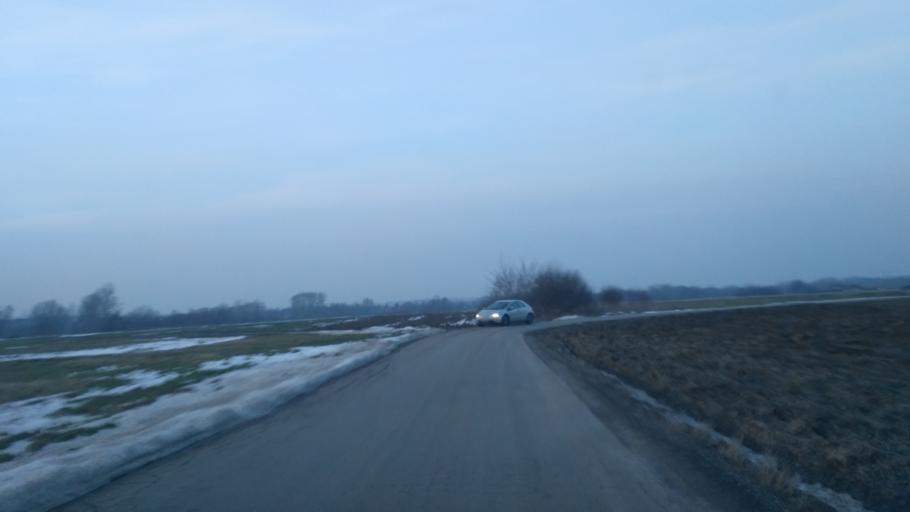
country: PL
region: Subcarpathian Voivodeship
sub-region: Powiat rzeszowski
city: Boguchwala
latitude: 49.9758
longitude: 21.9625
